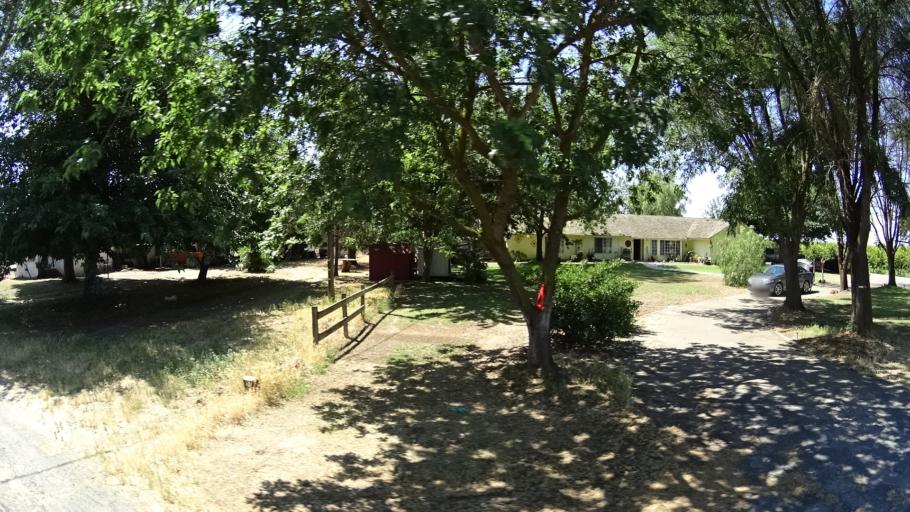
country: US
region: California
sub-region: Fresno County
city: Kingsburg
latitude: 36.4888
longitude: -119.5692
